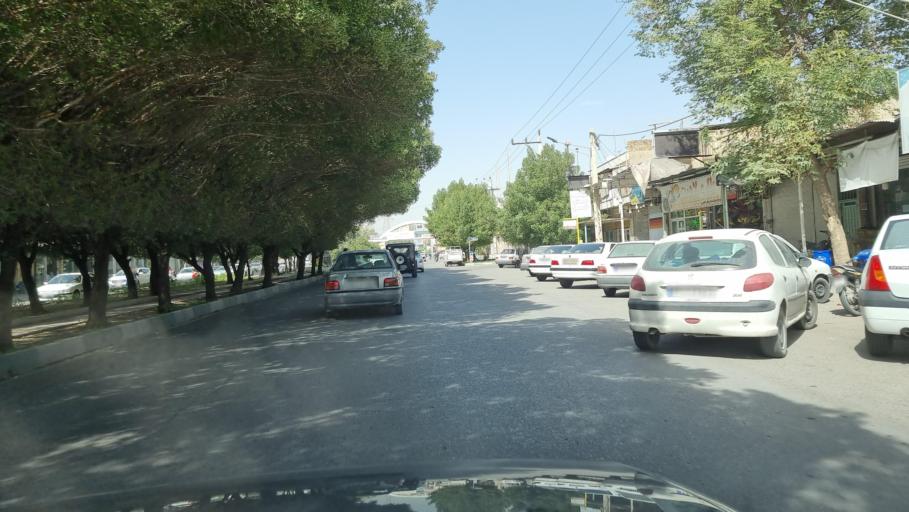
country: IR
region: Khuzestan
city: Dezful
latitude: 32.3861
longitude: 48.4121
